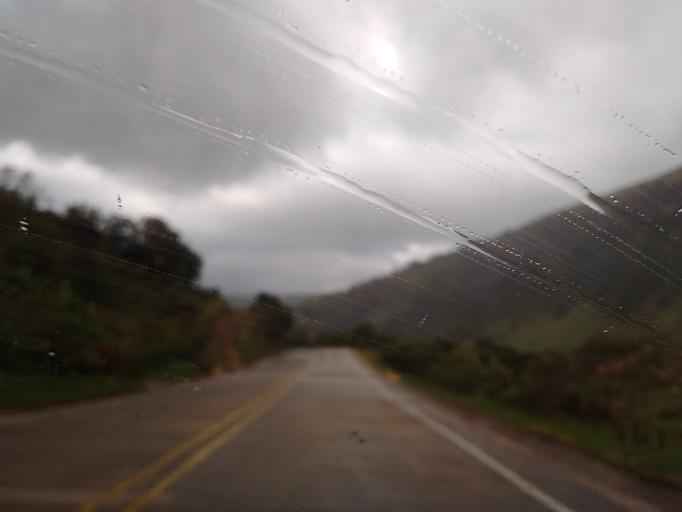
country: CO
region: Cauca
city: Paispamba
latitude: 2.3055
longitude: -76.5095
